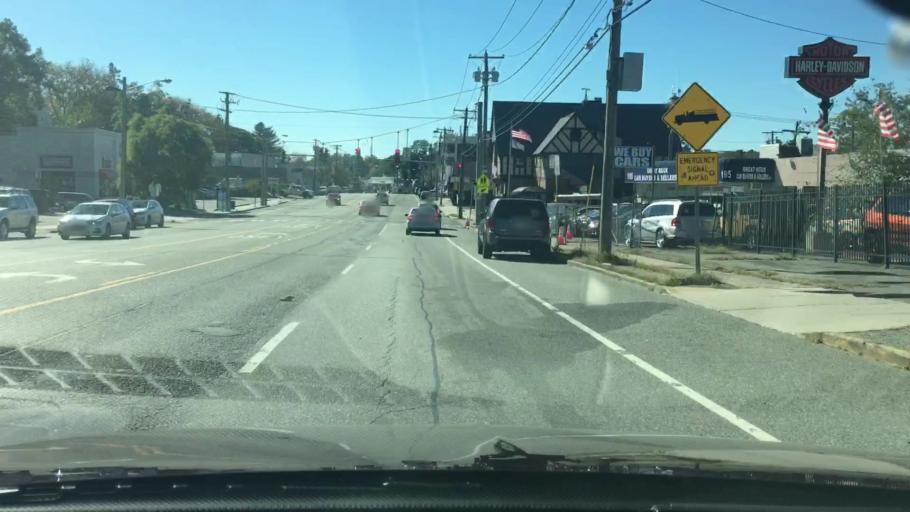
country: US
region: New York
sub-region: Nassau County
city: University Gardens
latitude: 40.7764
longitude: -73.7290
